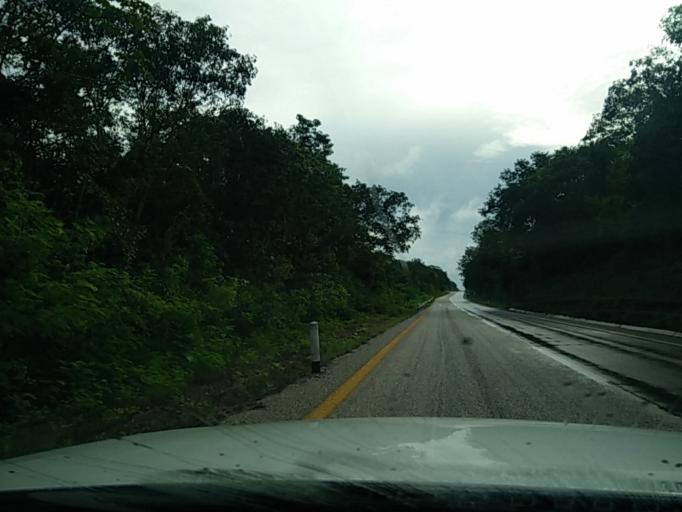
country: MX
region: Yucatan
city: Tunkas
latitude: 20.7556
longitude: -88.7473
